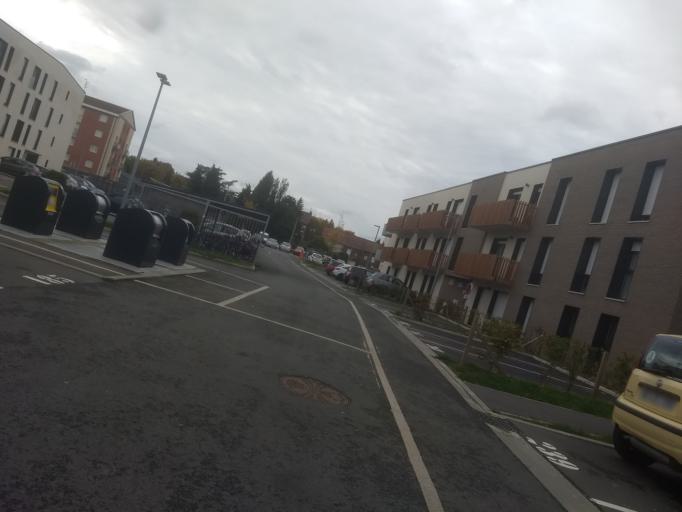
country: FR
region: Nord-Pas-de-Calais
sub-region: Departement du Pas-de-Calais
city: Arras
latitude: 50.2884
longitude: 2.7882
